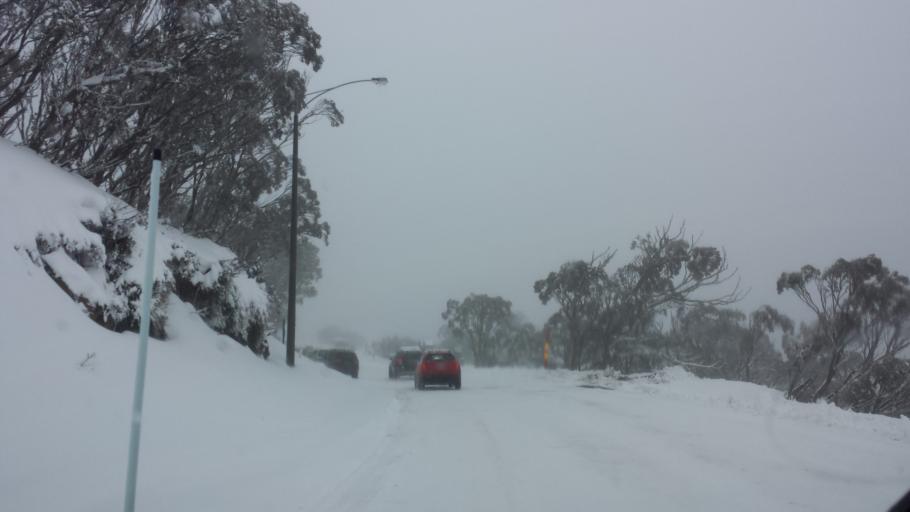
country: AU
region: Victoria
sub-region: Alpine
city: Mount Beauty
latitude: -36.9896
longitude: 147.1486
